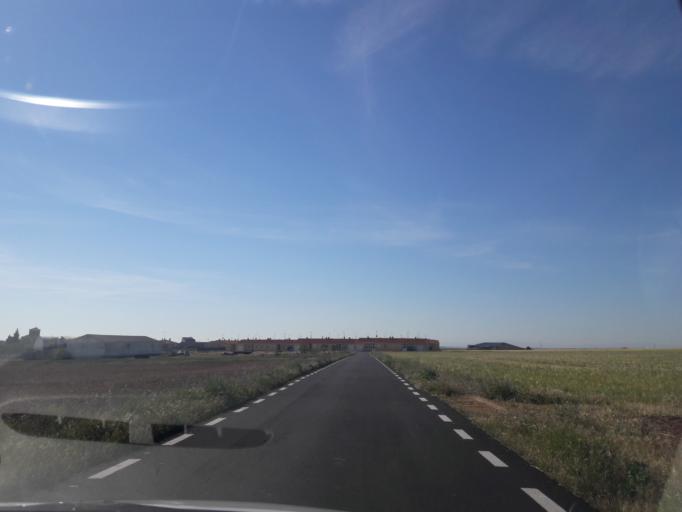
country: ES
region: Castille and Leon
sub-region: Provincia de Salamanca
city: Parada de Rubiales
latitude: 41.1494
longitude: -5.4425
